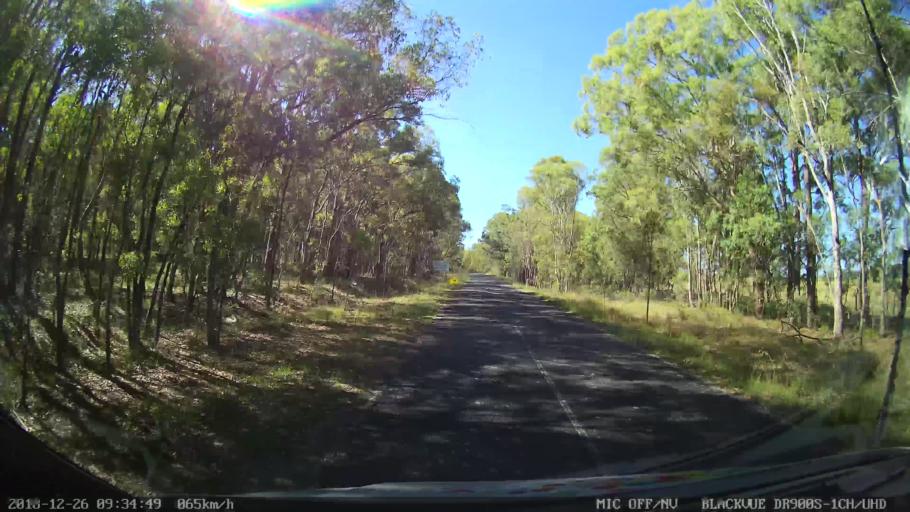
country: AU
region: New South Wales
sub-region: Mid-Western Regional
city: Kandos
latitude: -32.9091
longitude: 150.0382
